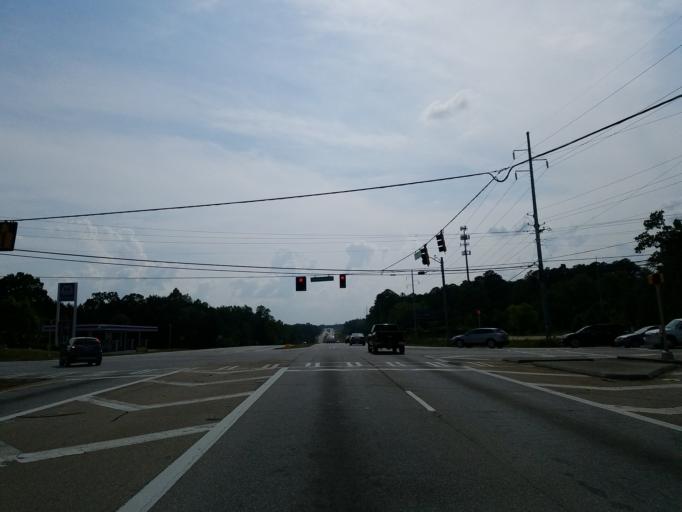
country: US
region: Georgia
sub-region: Paulding County
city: Hiram
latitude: 33.9264
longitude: -84.7476
